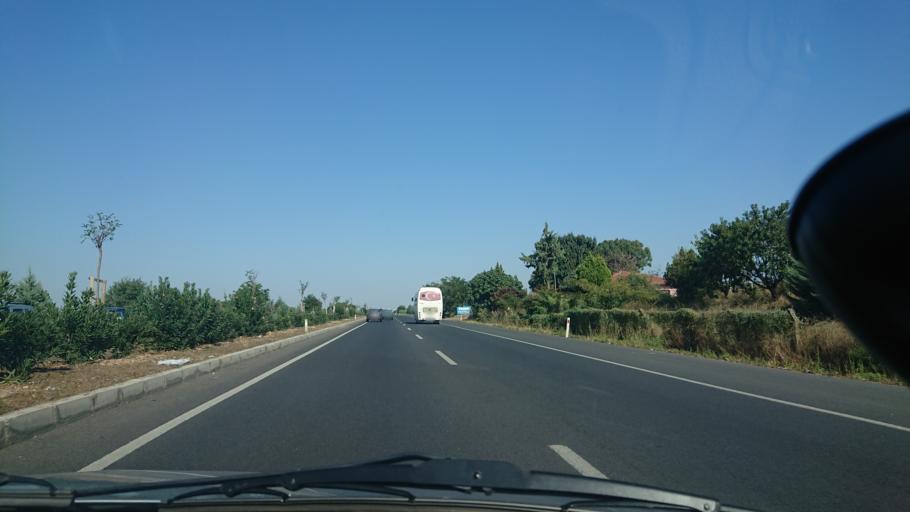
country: TR
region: Manisa
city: Ahmetli
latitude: 38.5056
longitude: 27.8857
